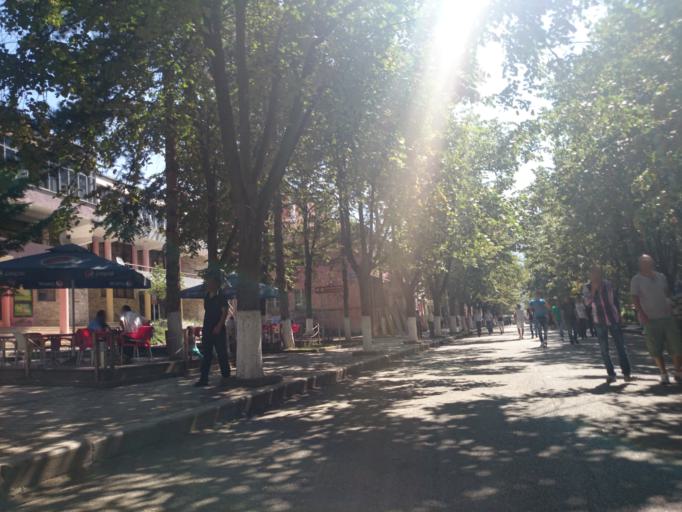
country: AL
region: Diber
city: Peshkopi
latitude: 41.6848
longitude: 20.4298
